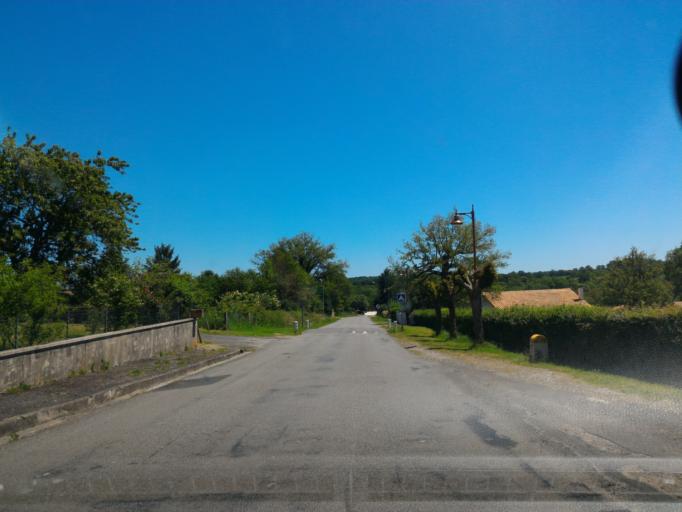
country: FR
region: Poitou-Charentes
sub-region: Departement de la Charente
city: Confolens
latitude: 46.0586
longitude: 0.7817
